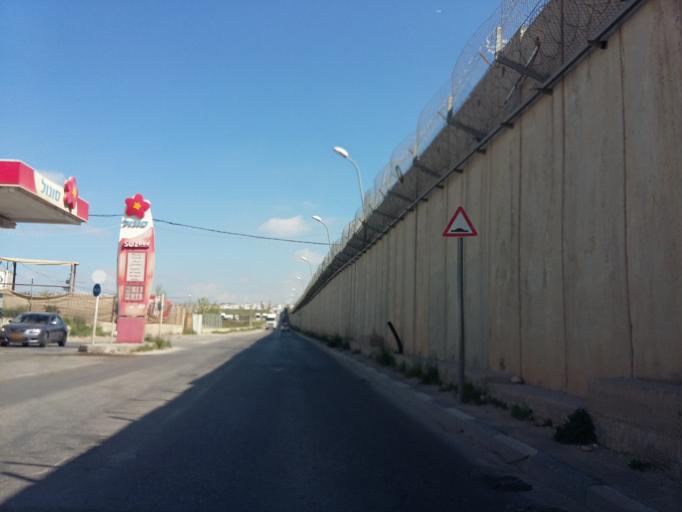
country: PS
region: West Bank
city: Ar Ram wa Dahiyat al Barid
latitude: 31.8550
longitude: 35.2247
